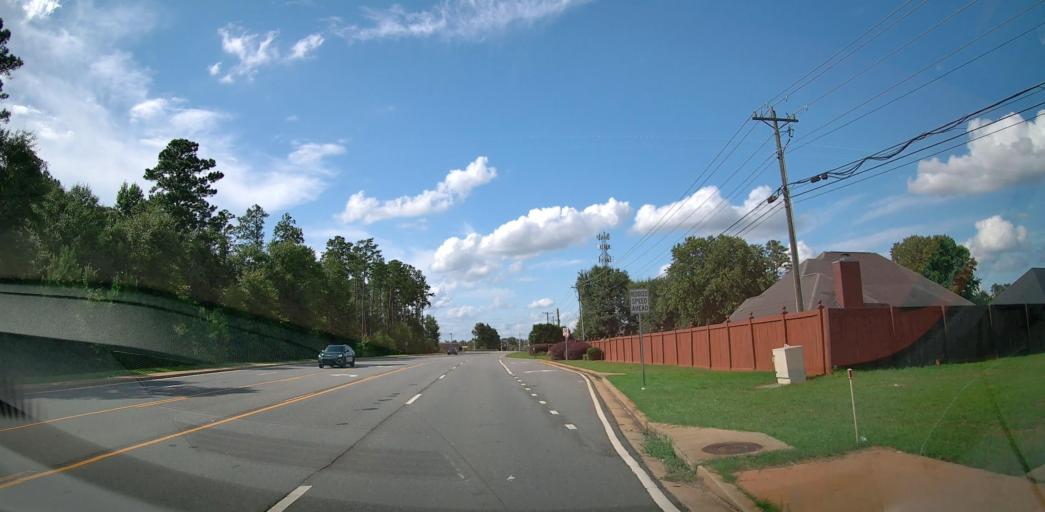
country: US
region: Georgia
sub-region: Houston County
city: Centerville
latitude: 32.5449
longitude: -83.6909
